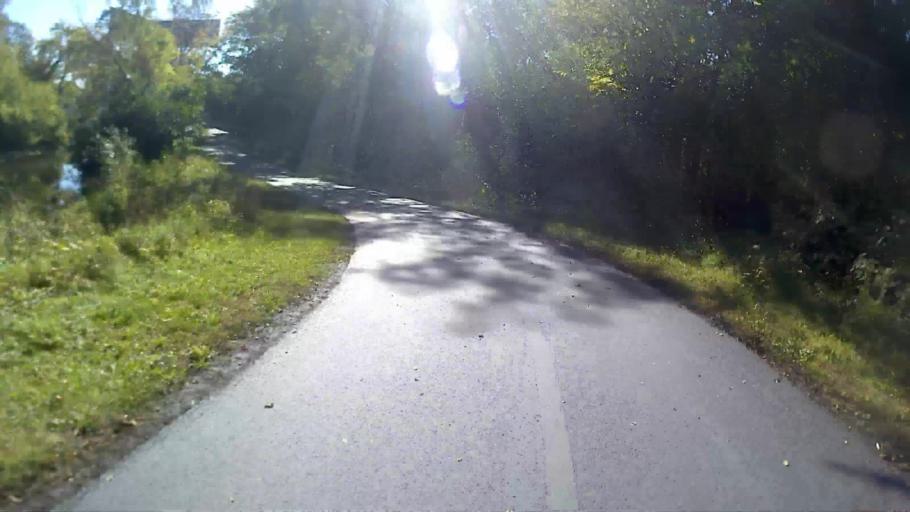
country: US
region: Illinois
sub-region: DuPage County
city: Villa Park
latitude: 41.9071
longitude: -87.9680
